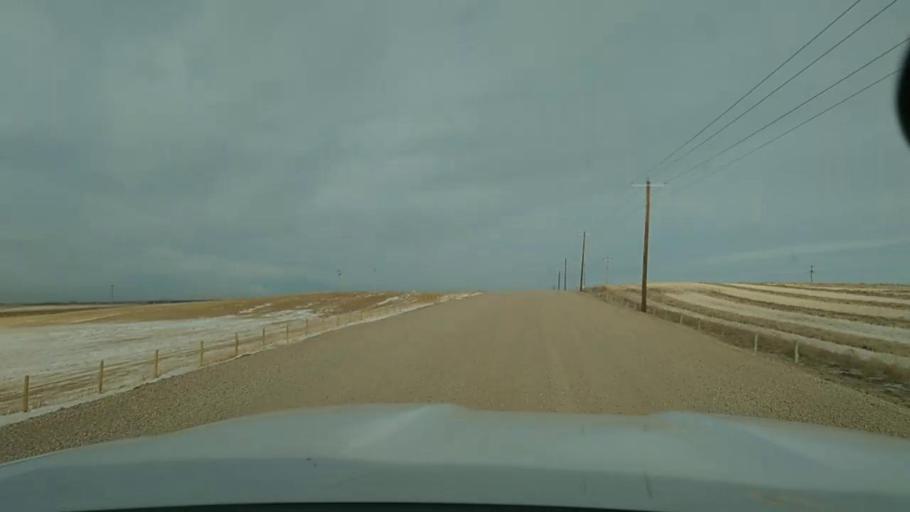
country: CA
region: Alberta
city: Airdrie
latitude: 51.2394
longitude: -113.9118
